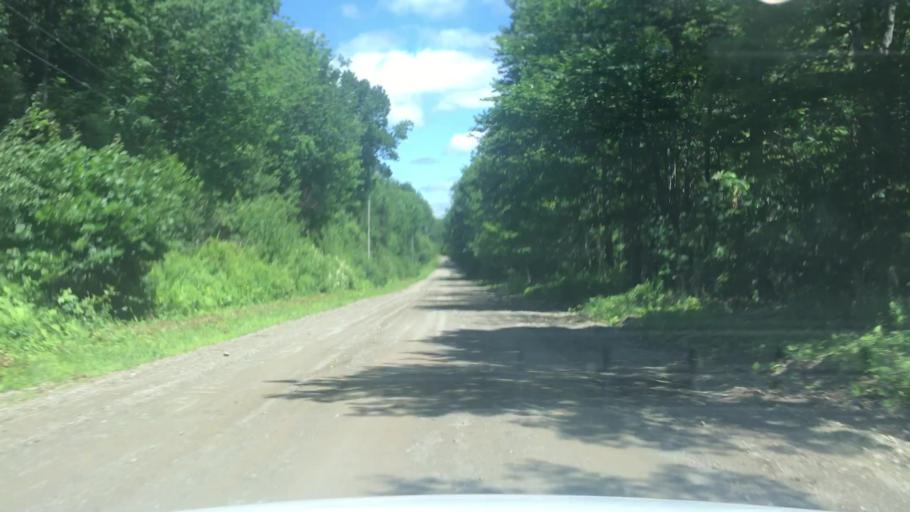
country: US
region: Maine
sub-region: Waldo County
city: Searsmont
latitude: 44.4645
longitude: -69.3053
